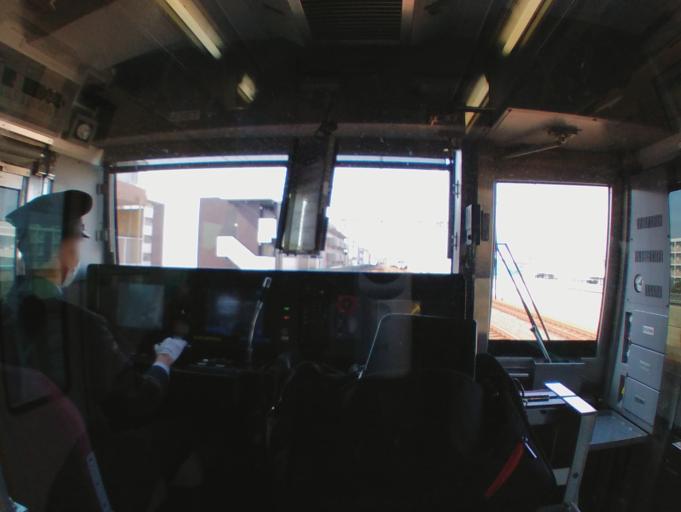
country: JP
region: Tokyo
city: Mitaka-shi
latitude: 35.6477
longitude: 139.6240
